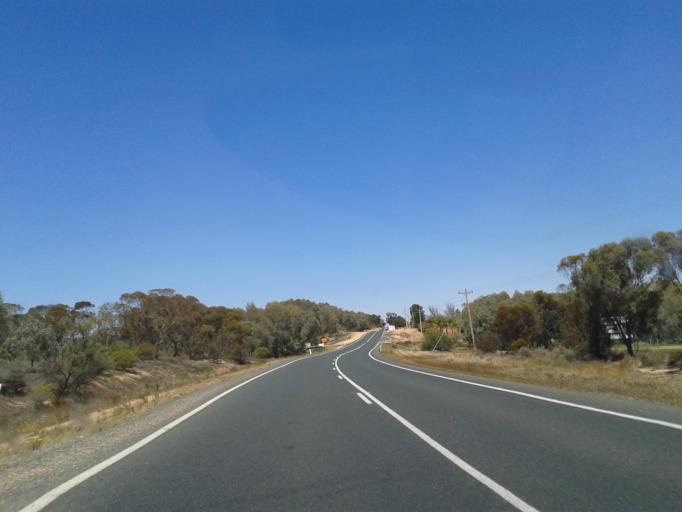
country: AU
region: New South Wales
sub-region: Wentworth
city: Gol Gol
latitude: -34.2390
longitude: 142.2494
